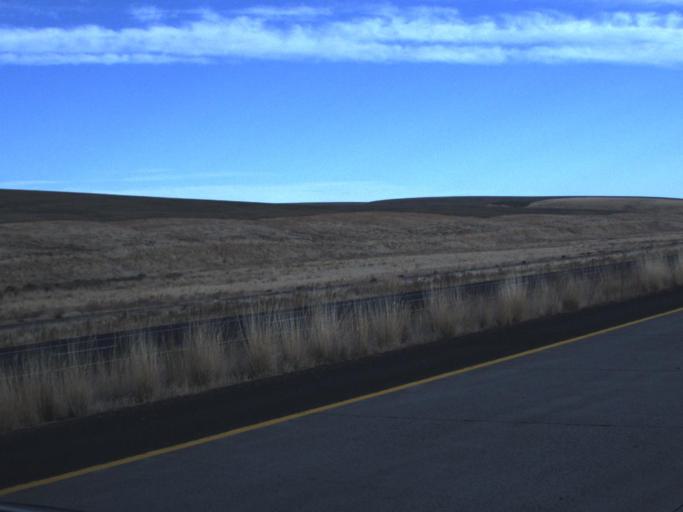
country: US
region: Washington
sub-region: Franklin County
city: Connell
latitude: 46.8528
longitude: -118.6384
